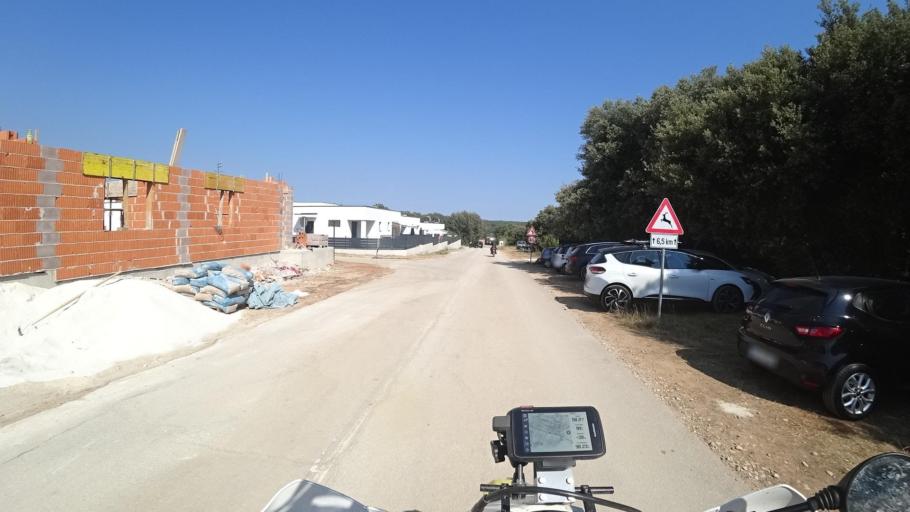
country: HR
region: Istarska
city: Fazana
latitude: 44.9890
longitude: 13.7526
